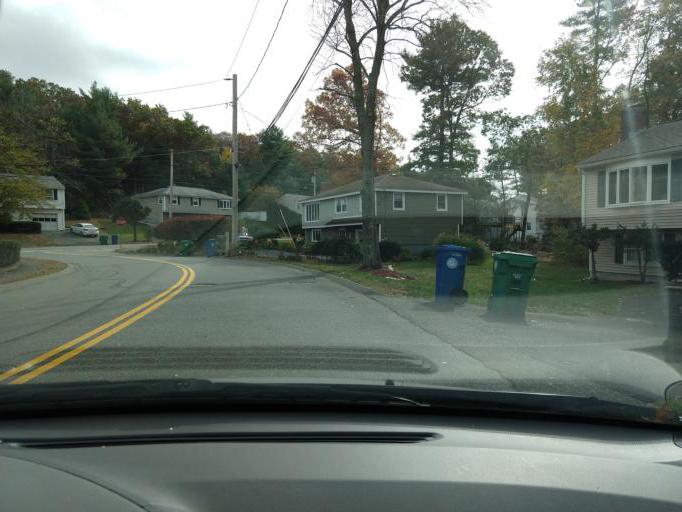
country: US
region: Massachusetts
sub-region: Middlesex County
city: Burlington
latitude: 42.5202
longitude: -71.1971
